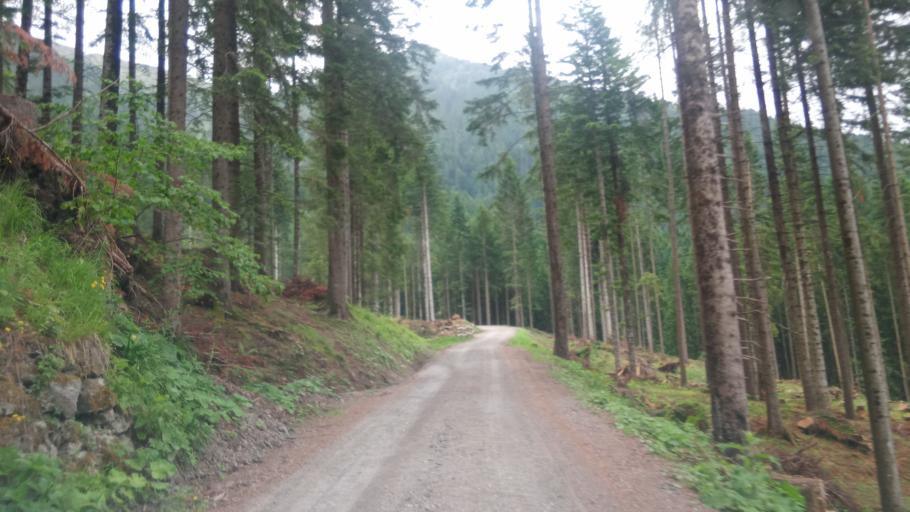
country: IT
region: Friuli Venezia Giulia
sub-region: Provincia di Udine
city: Paluzza
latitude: 46.5685
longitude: 13.0180
